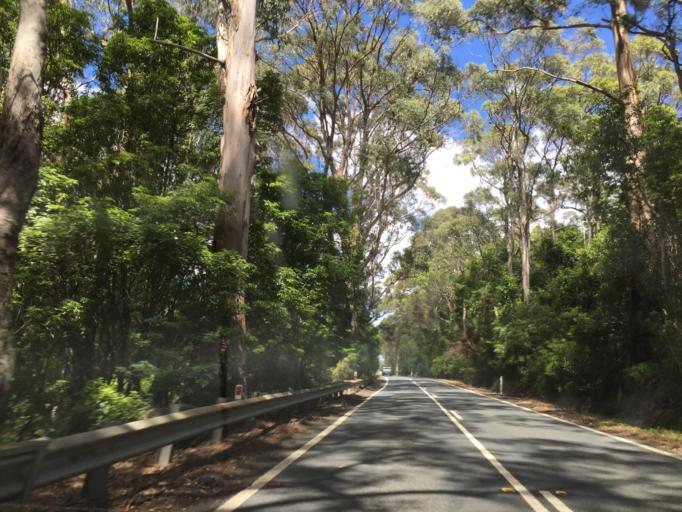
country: AU
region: New South Wales
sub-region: Blue Mountains Municipality
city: Lawson
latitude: -33.5250
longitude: 150.4588
